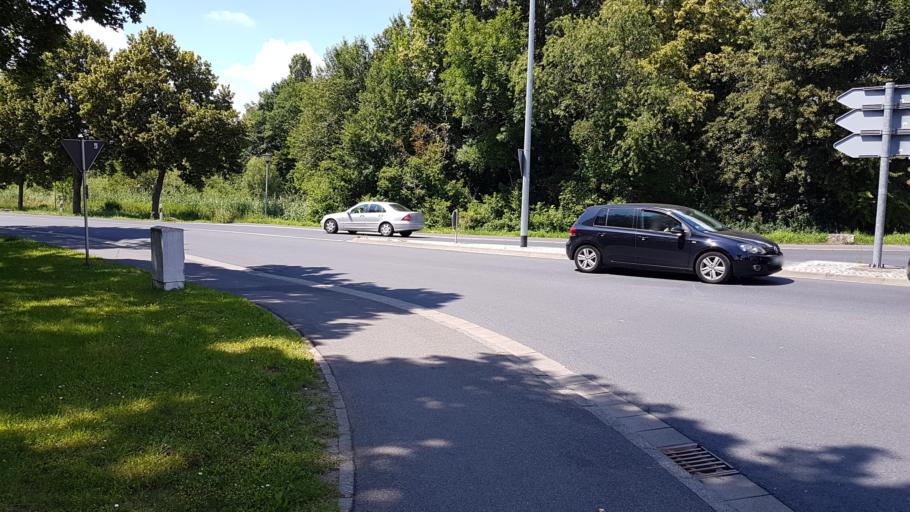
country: DE
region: Bavaria
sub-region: Regierungsbezirk Unterfranken
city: Schwebheim
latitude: 49.9935
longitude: 10.2464
